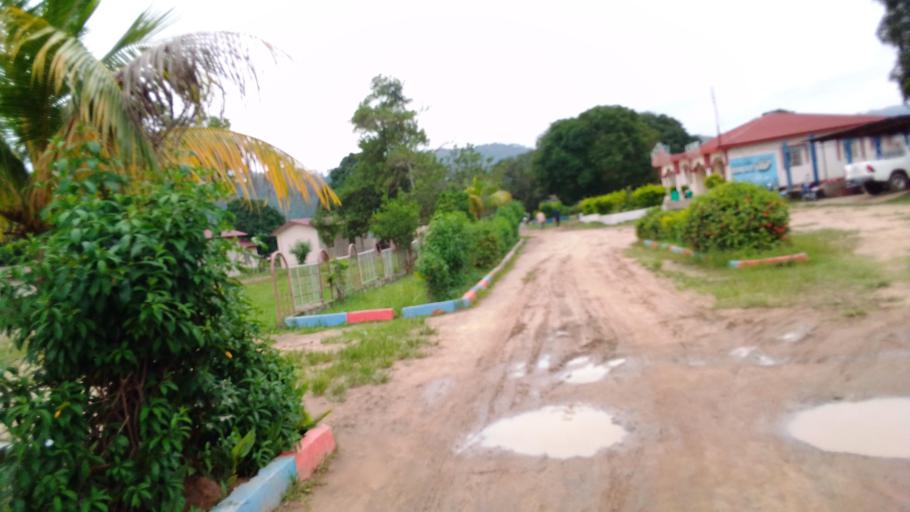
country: SL
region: Eastern Province
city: Kenema
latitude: 7.8617
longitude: -11.2020
